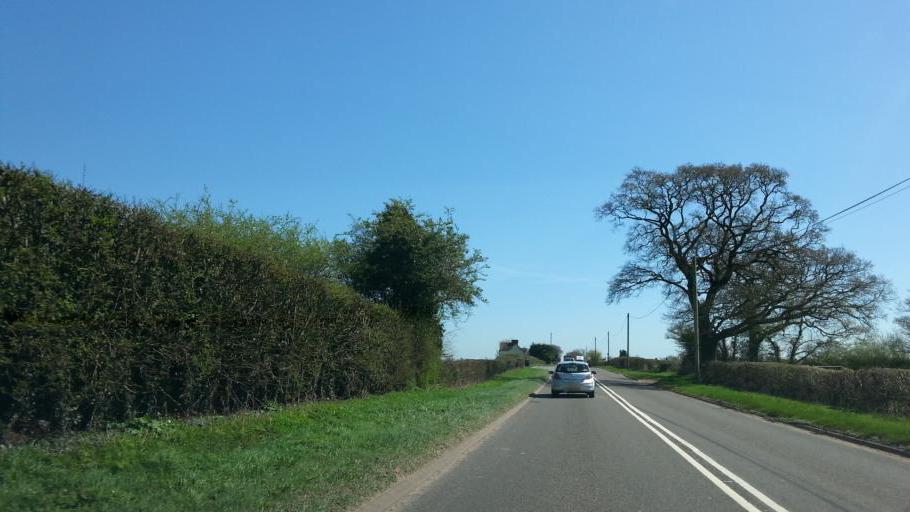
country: GB
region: England
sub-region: Staffordshire
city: Wheaton Aston
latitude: 52.6940
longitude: -2.2288
